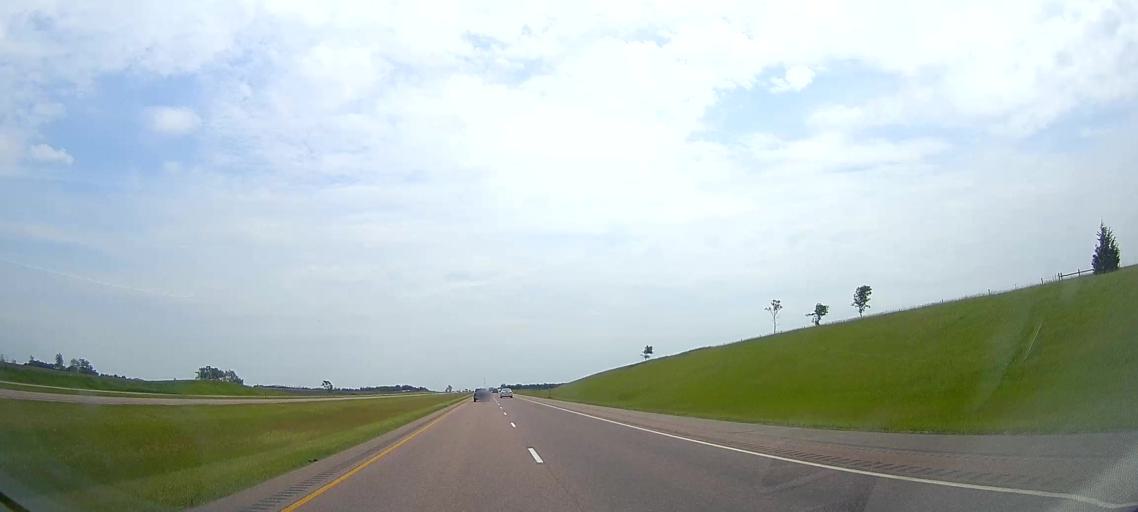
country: US
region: South Dakota
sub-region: Minnehaha County
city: Hartford
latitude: 43.6571
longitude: -97.1071
